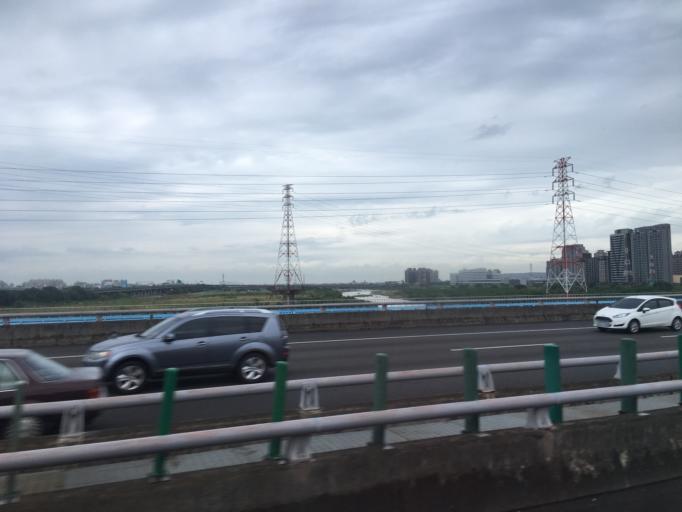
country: TW
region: Taiwan
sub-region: Hsinchu
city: Zhubei
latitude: 24.8123
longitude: 121.0118
